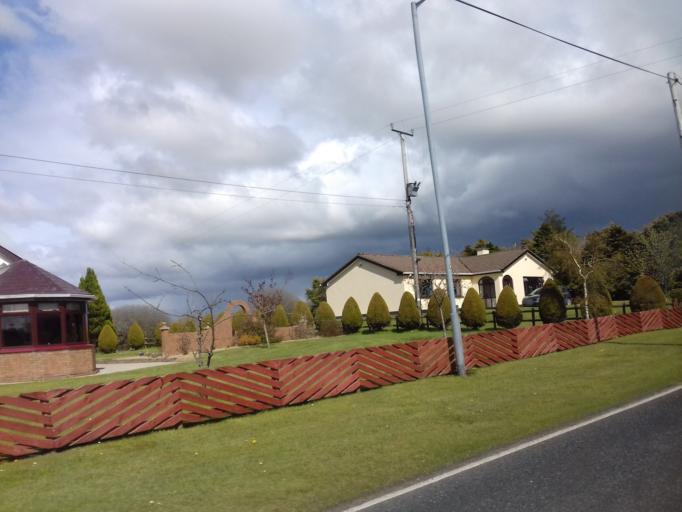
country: IE
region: Ulster
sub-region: County Donegal
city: Ballyshannon
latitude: 54.4716
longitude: -8.0667
